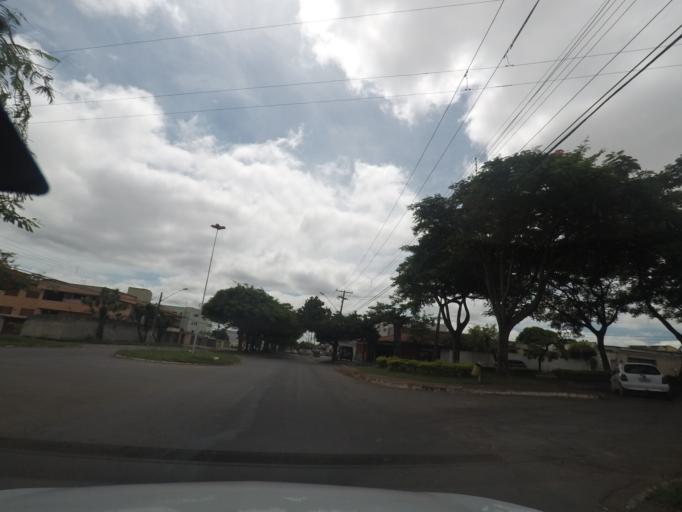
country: BR
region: Goias
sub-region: Goiania
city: Goiania
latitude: -16.6743
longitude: -49.2345
